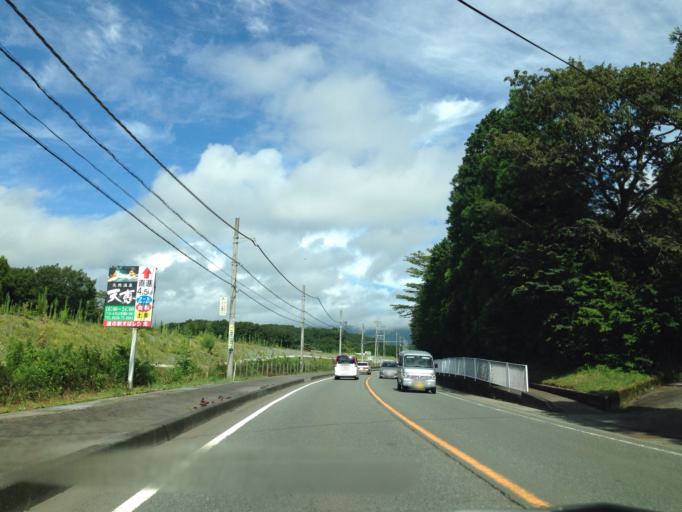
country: JP
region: Shizuoka
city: Gotemba
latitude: 35.3402
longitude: 138.8887
